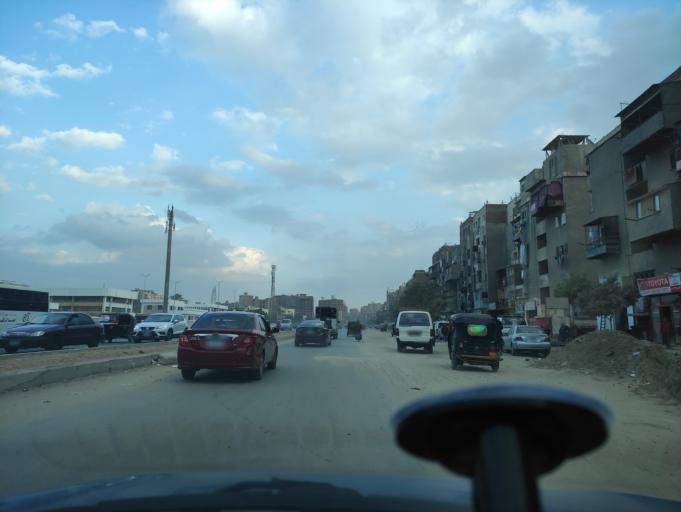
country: EG
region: Muhafazat al Qalyubiyah
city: Al Khankah
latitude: 30.1365
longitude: 31.3511
